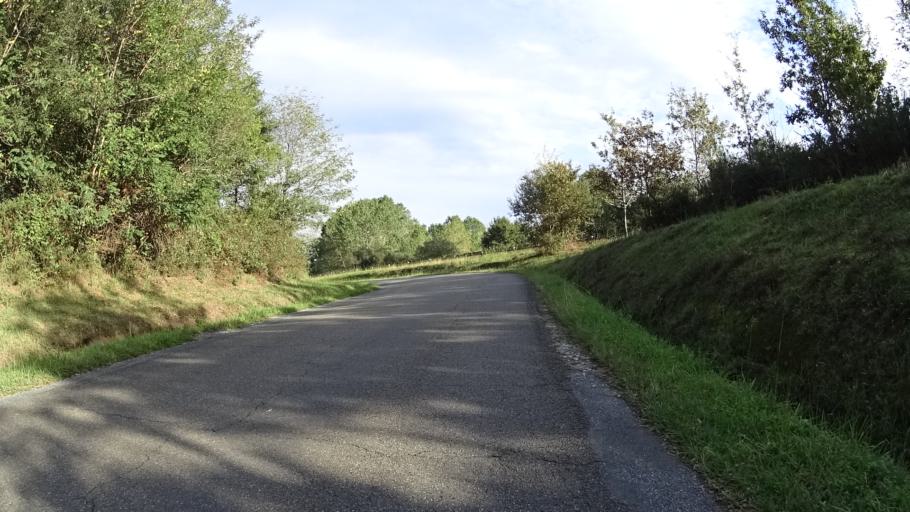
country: FR
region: Aquitaine
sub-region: Departement des Landes
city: Saint-Paul-les-Dax
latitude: 43.7420
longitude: -1.0728
